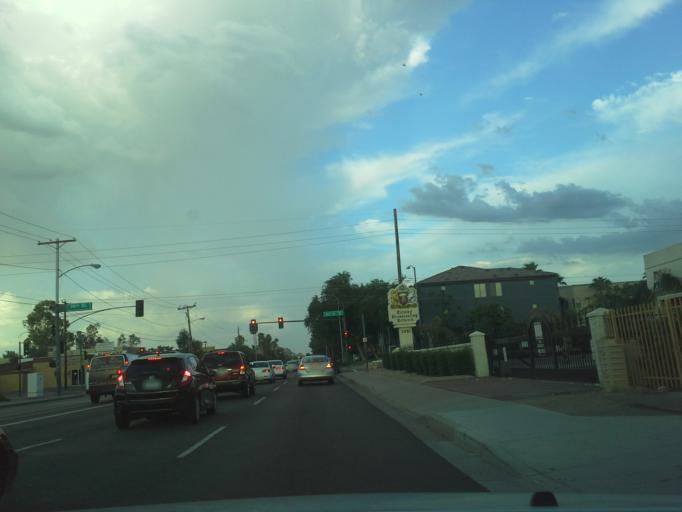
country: US
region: Arizona
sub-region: Maricopa County
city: Phoenix
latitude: 33.4657
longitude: -112.0050
